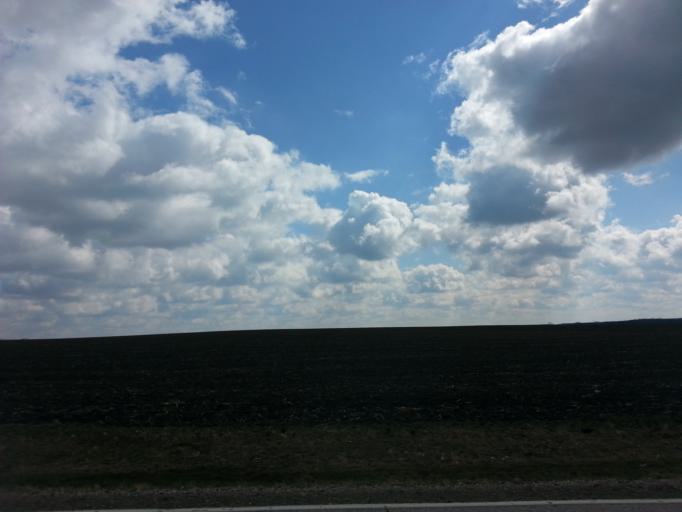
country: US
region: Minnesota
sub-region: Dodge County
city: Mantorville
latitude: 44.0944
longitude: -92.7022
